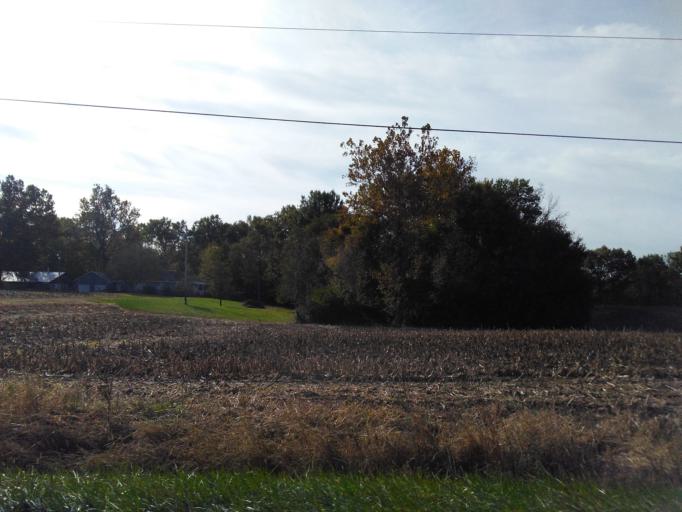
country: US
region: Illinois
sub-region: Madison County
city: Troy
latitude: 38.7178
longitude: -89.8710
